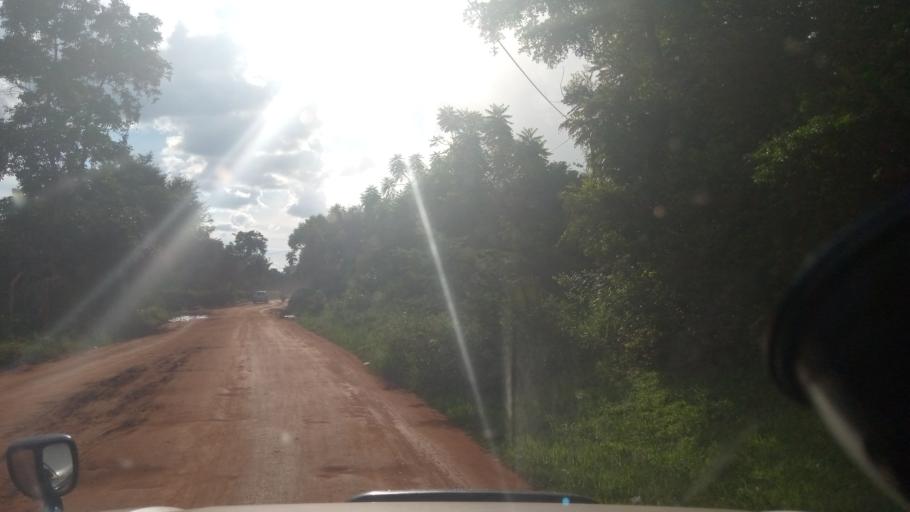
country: UG
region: Northern Region
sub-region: Lira District
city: Lira
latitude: 2.2281
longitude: 32.9027
